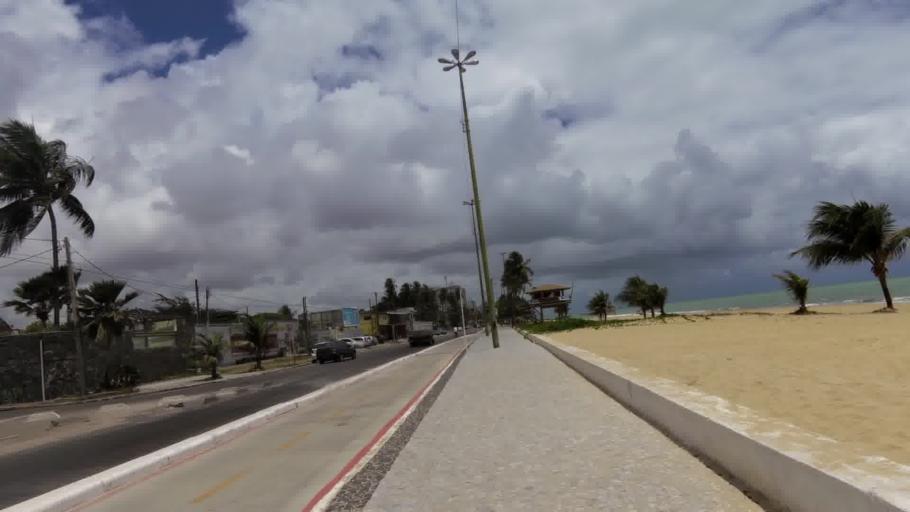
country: BR
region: Pernambuco
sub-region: Jaboatao Dos Guararapes
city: Jaboatao
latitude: -8.1603
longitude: -34.9115
